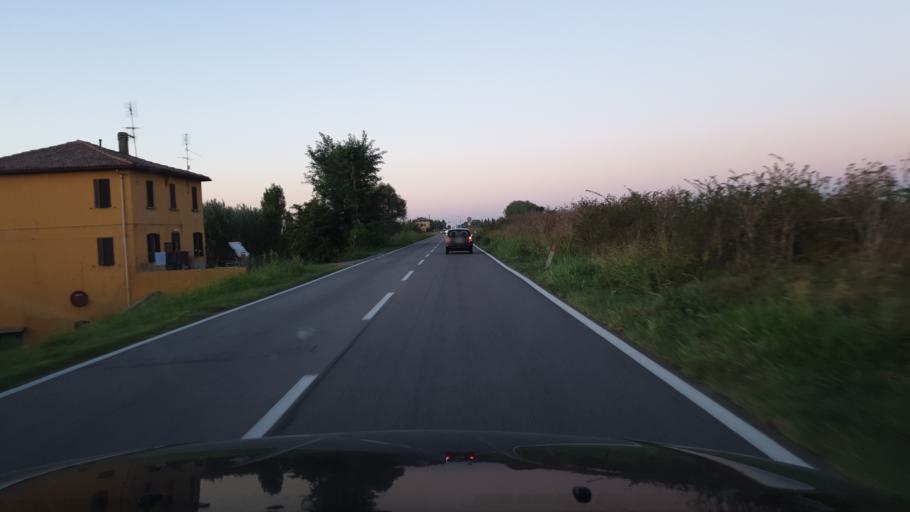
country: IT
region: Emilia-Romagna
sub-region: Provincia di Bologna
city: Minerbio
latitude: 44.6356
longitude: 11.4688
